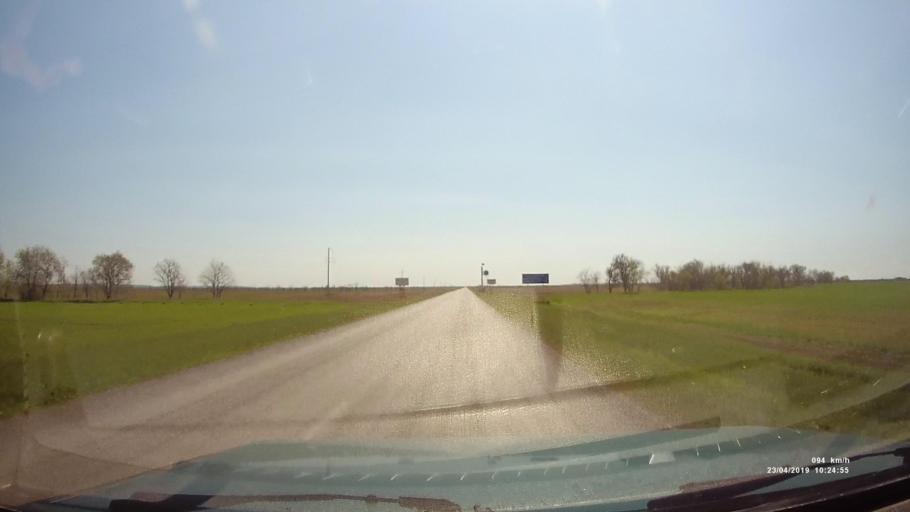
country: RU
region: Rostov
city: Sovetskoye
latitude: 46.6350
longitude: 42.4493
